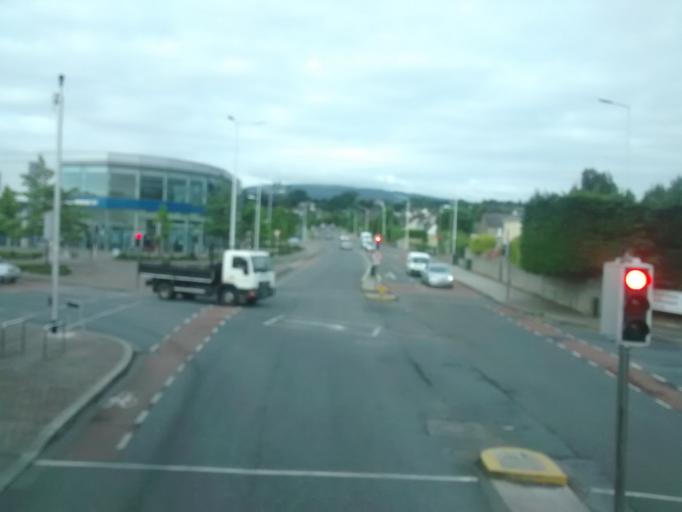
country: IE
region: Leinster
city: Cabinteely
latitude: 53.2785
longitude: -6.1634
